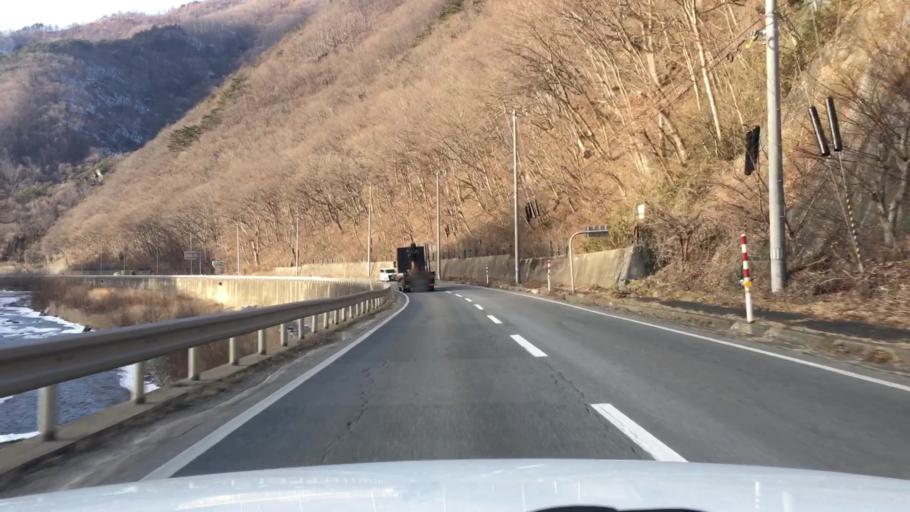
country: JP
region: Iwate
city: Tono
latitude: 39.6484
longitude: 141.5856
